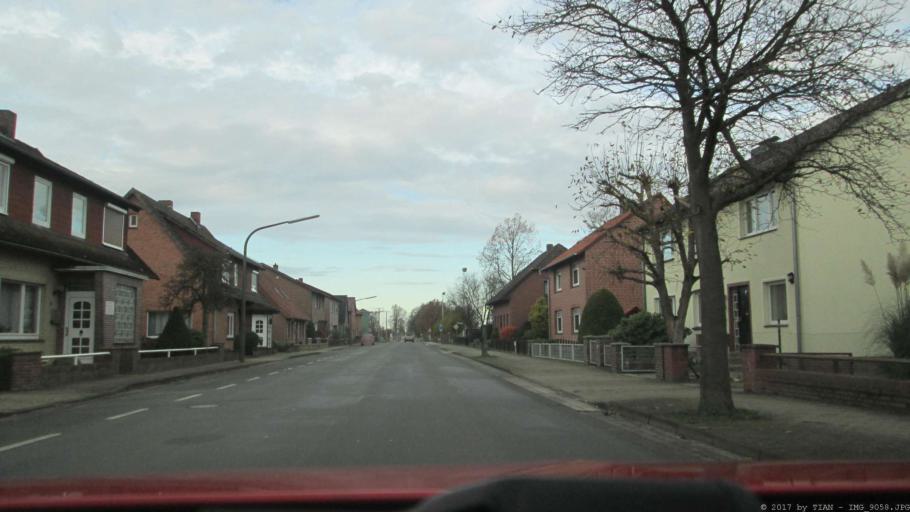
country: DE
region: Lower Saxony
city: Wittingen
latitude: 52.6846
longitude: 10.7022
